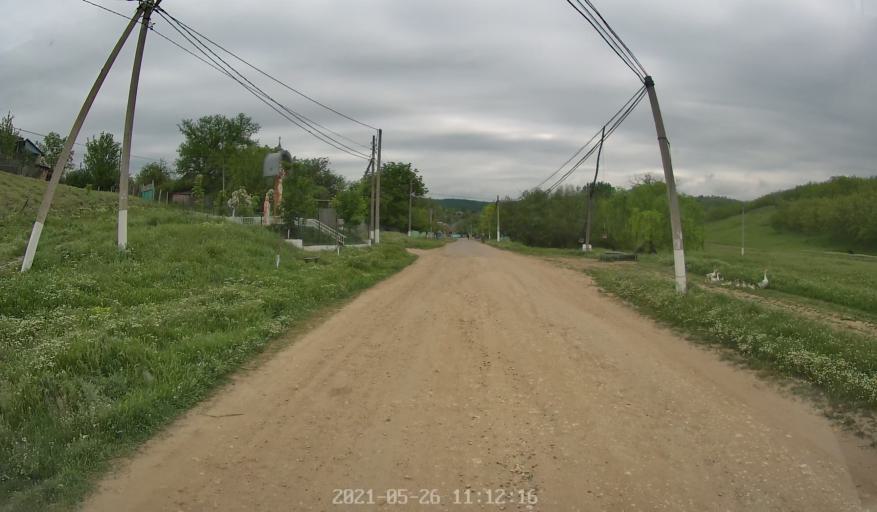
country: MD
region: Hincesti
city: Dancu
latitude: 46.8231
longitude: 28.3806
